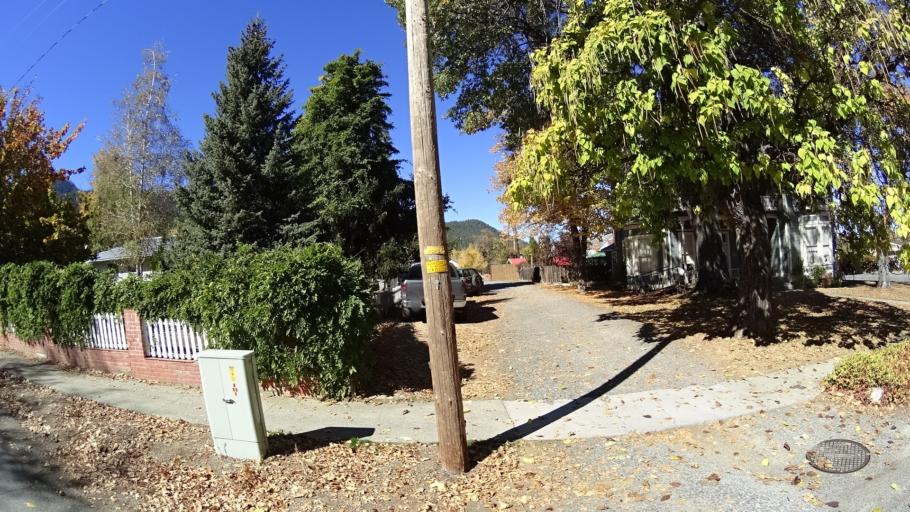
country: US
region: California
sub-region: Siskiyou County
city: Yreka
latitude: 41.4556
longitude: -122.8952
